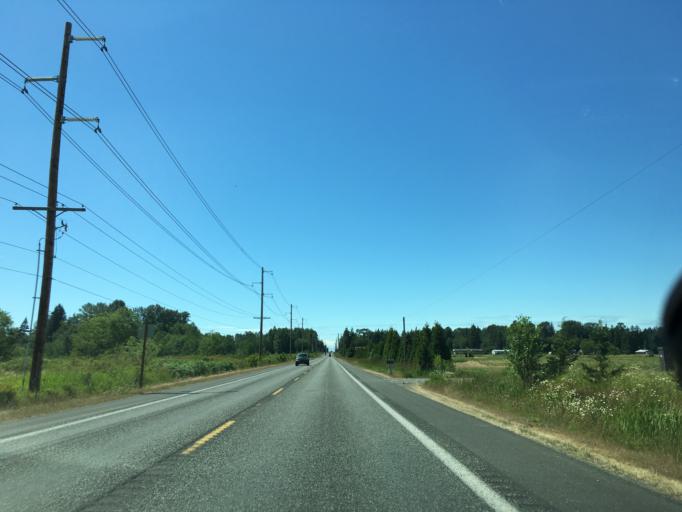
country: US
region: Washington
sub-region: Whatcom County
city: Birch Bay
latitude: 48.9357
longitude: -122.6955
